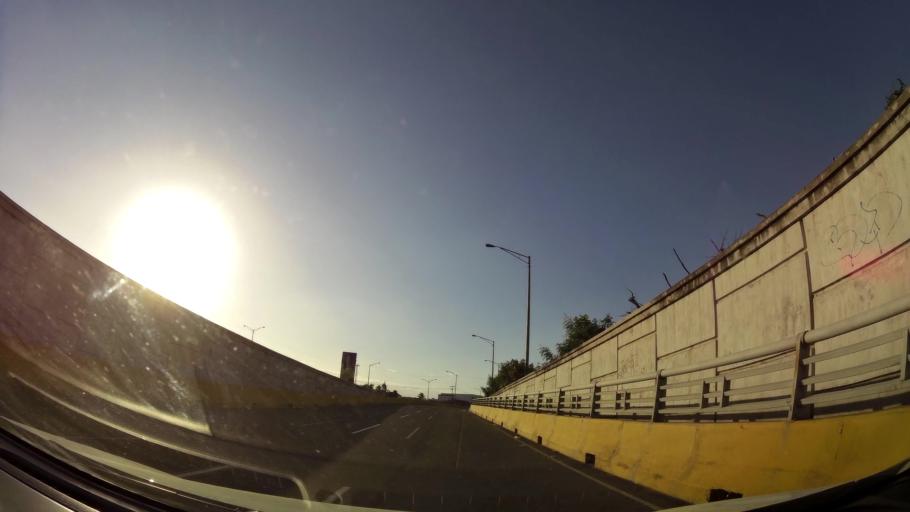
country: DO
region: Santo Domingo
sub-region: Santo Domingo
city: Santo Domingo Este
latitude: 18.4718
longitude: -69.8314
